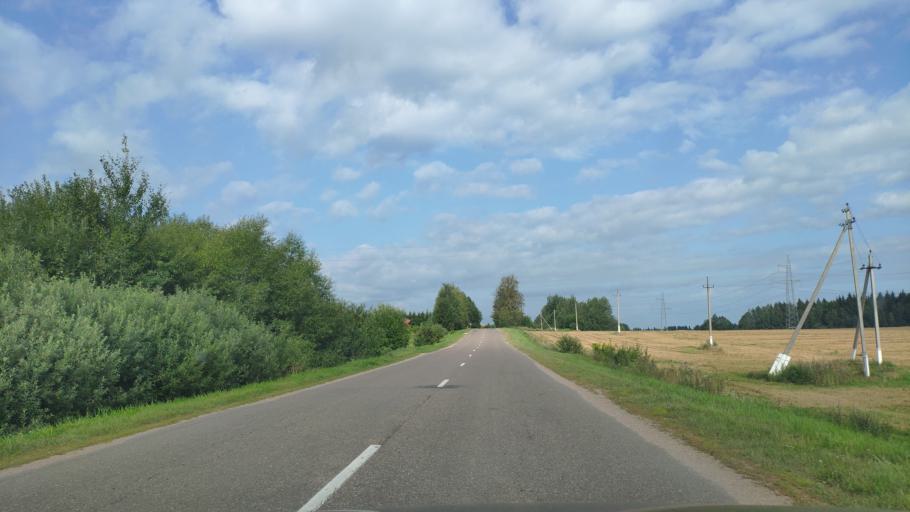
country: BY
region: Minsk
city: Khatsyezhyna
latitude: 53.8726
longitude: 27.3039
